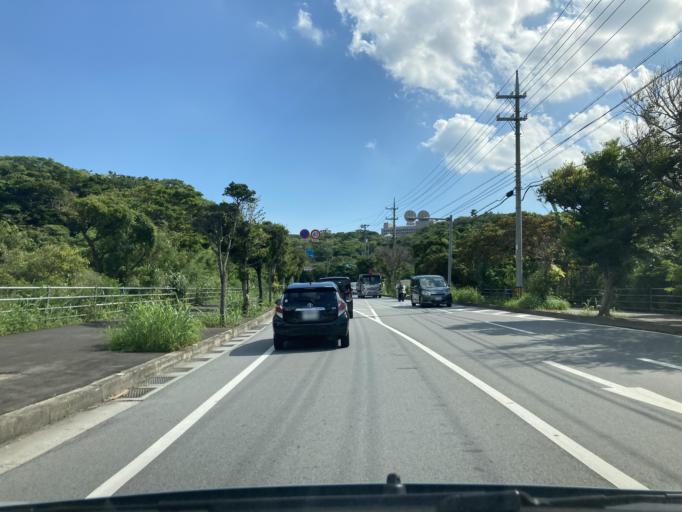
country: JP
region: Okinawa
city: Ginowan
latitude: 26.2479
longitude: 127.7575
